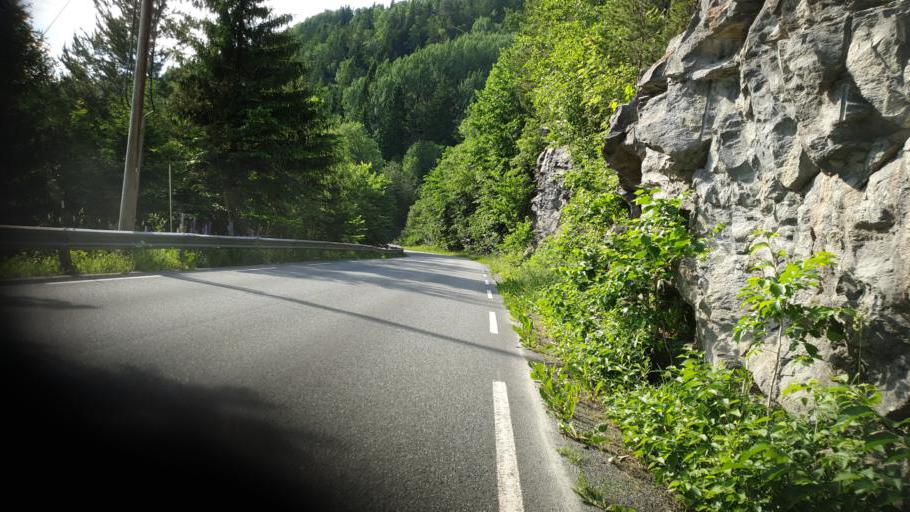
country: NO
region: Sor-Trondelag
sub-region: Trondheim
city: Trondheim
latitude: 63.5567
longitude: 10.2458
